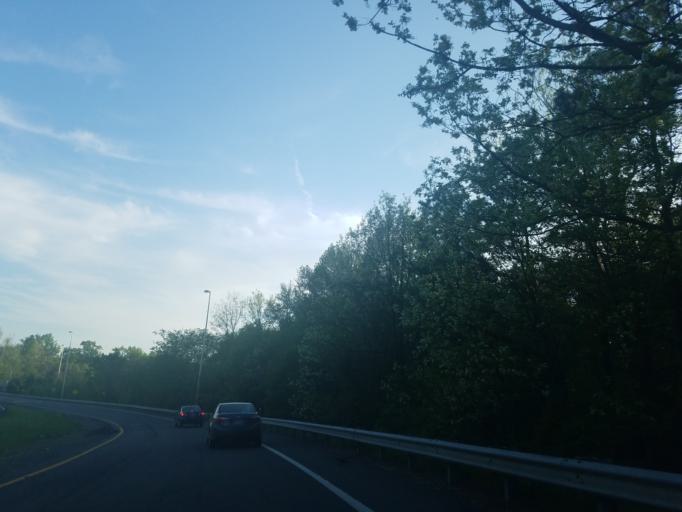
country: US
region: Virginia
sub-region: Fairfax County
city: Centreville
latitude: 38.8384
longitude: -77.4484
